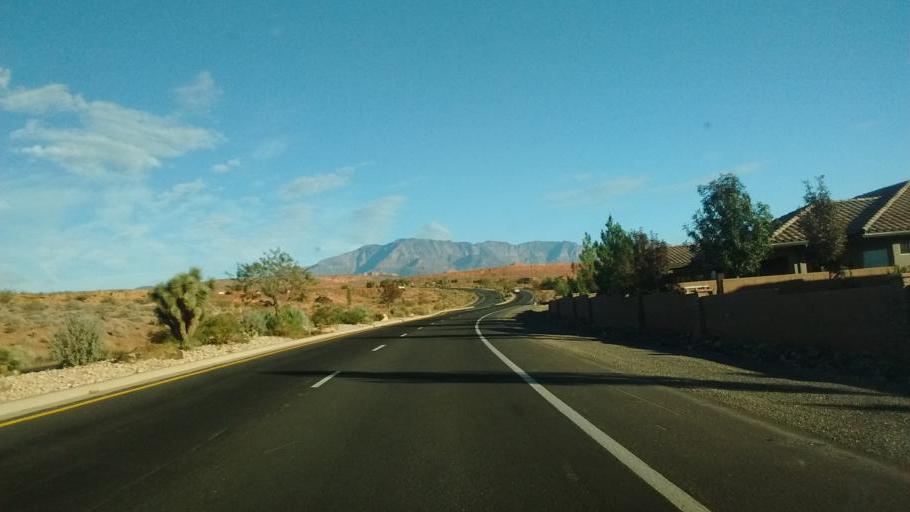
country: US
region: Utah
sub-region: Washington County
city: Washington
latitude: 37.1389
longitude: -113.4856
